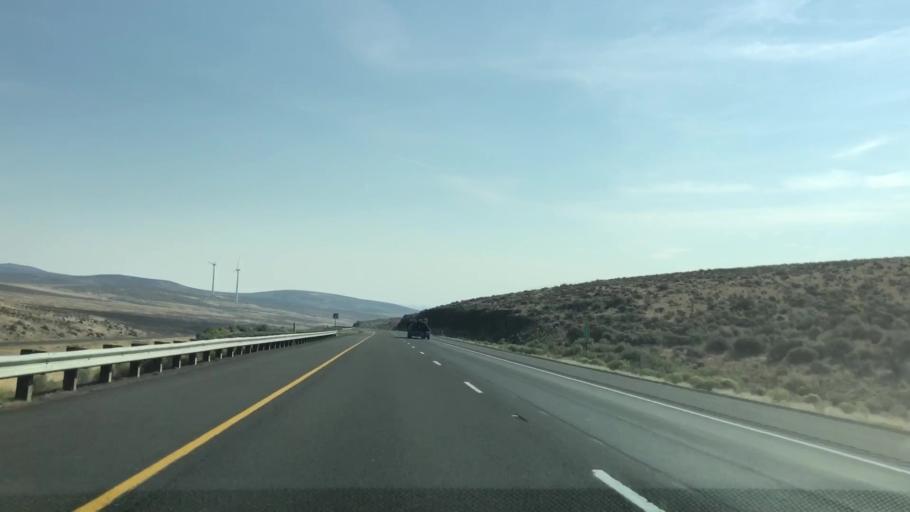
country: US
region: Washington
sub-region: Grant County
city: Mattawa
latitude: 46.9394
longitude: -120.1214
